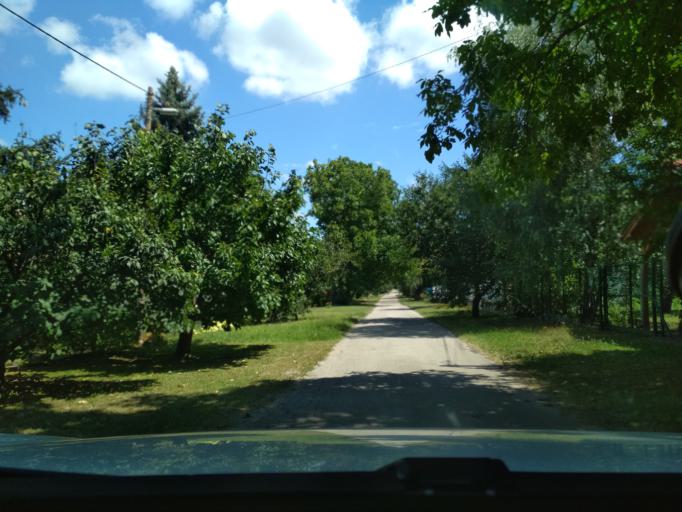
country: HU
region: Fejer
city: Gardony
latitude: 47.2119
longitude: 18.6492
